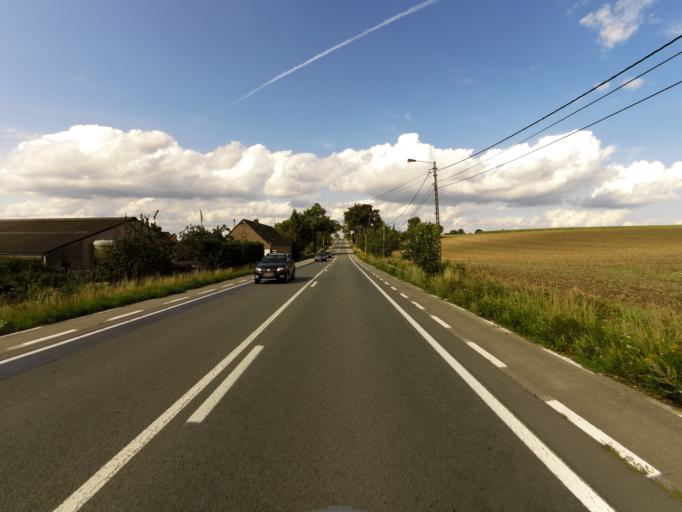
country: BE
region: Flanders
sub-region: Provincie Oost-Vlaanderen
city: Ronse
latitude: 50.7085
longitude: 3.5800
